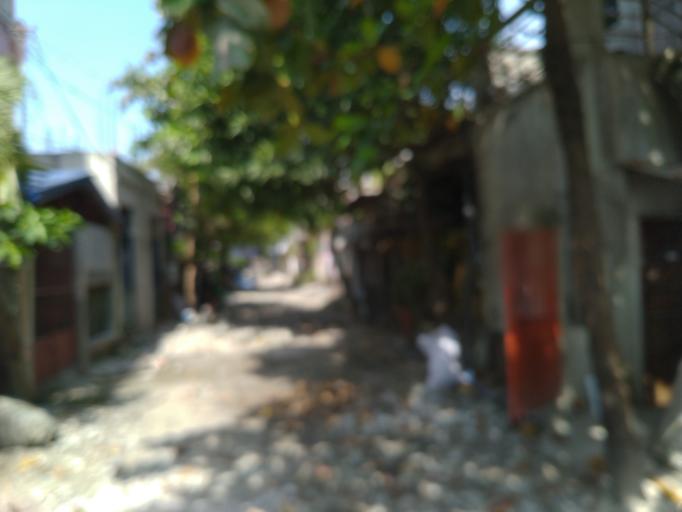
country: PH
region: Calabarzon
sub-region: Province of Rizal
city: Taytay
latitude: 14.5361
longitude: 121.1117
